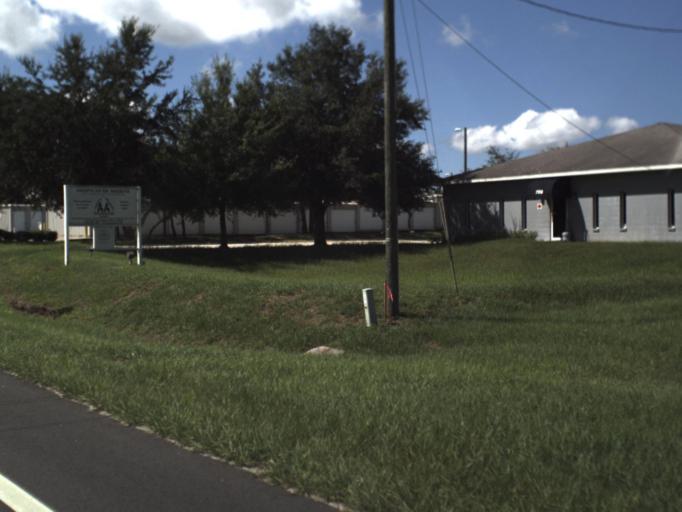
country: US
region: Florida
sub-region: Polk County
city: Haines City
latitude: 28.1174
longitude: -81.6180
